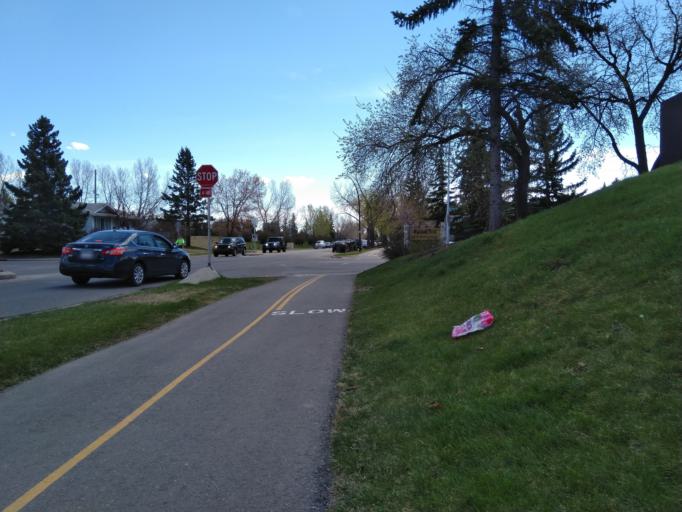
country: CA
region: Alberta
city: Calgary
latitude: 51.0164
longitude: -114.1598
